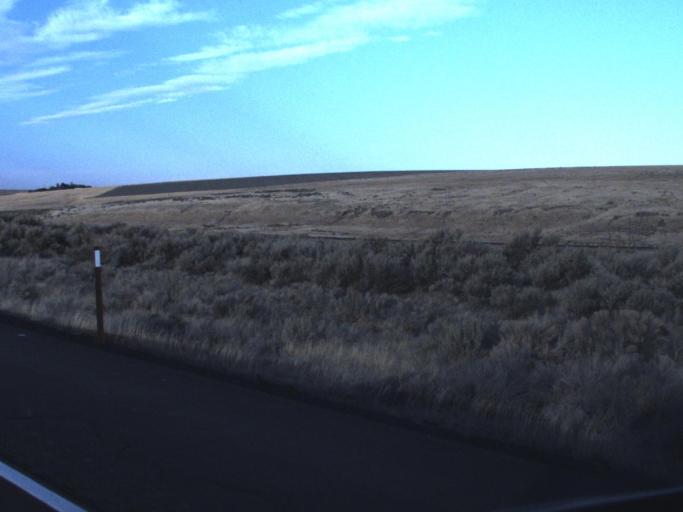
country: US
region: Washington
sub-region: Adams County
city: Ritzville
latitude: 47.0049
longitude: -118.5275
